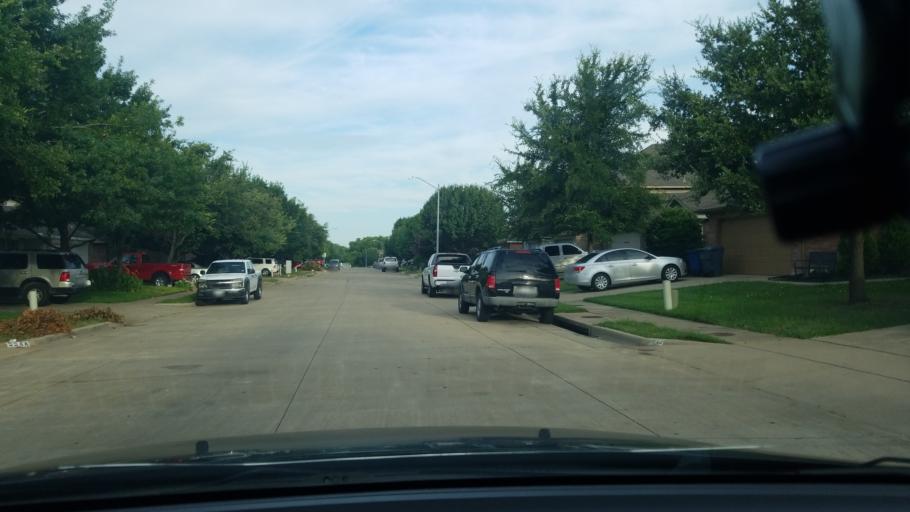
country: US
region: Texas
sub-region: Dallas County
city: Balch Springs
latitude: 32.7655
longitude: -96.6492
